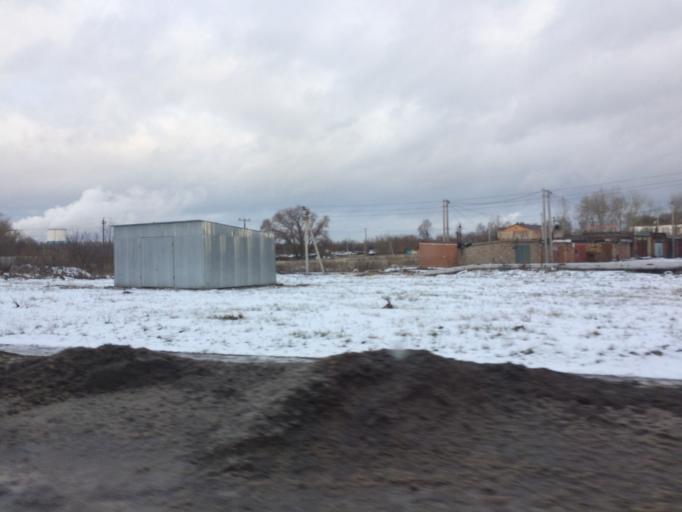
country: RU
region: Tula
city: Suvorov
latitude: 54.1245
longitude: 36.4869
